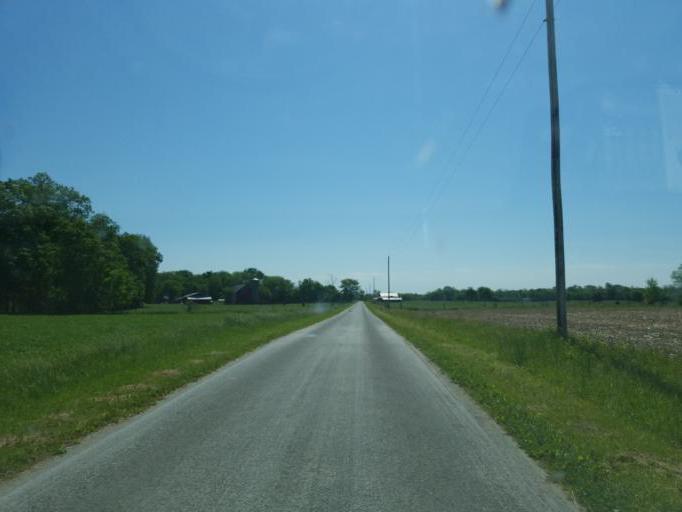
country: US
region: Ohio
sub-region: Hardin County
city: Kenton
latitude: 40.6173
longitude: -83.4885
